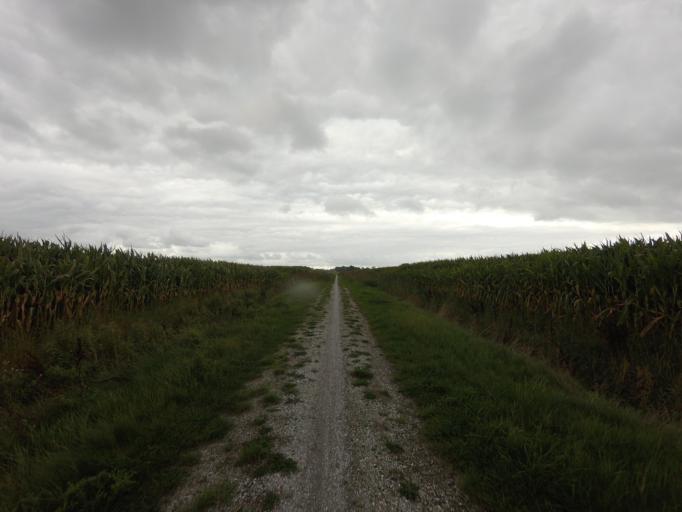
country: NL
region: Friesland
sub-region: Gemeente Weststellingwerf
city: Noordwolde
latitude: 52.9407
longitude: 6.1873
